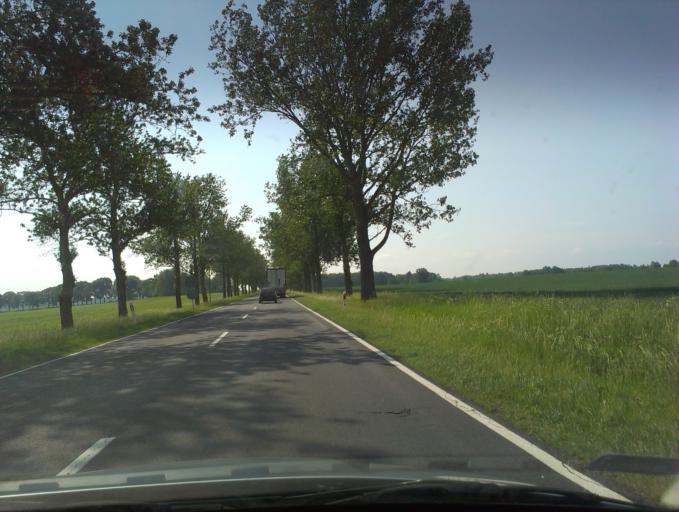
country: PL
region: Greater Poland Voivodeship
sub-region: Powiat zlotowski
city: Okonek
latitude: 53.5949
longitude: 16.8148
